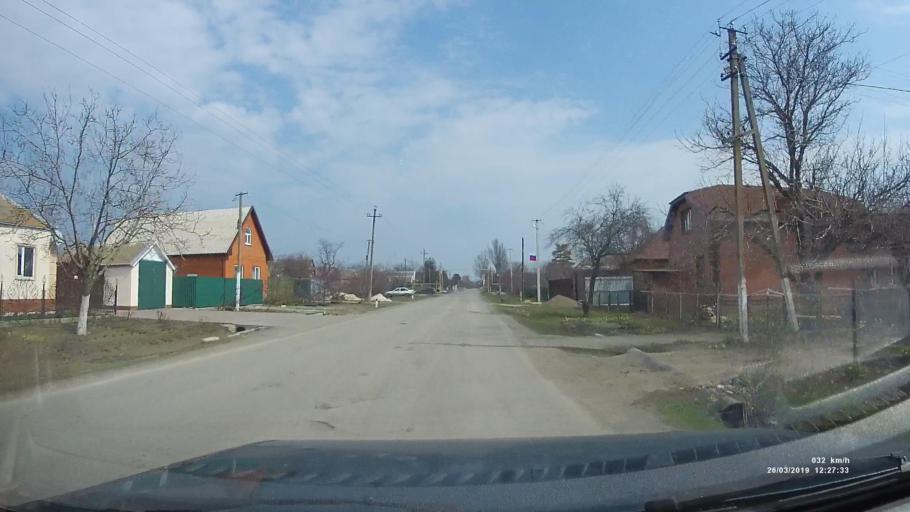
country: RU
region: Rostov
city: Novobessergenovka
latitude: 47.1556
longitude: 38.6798
